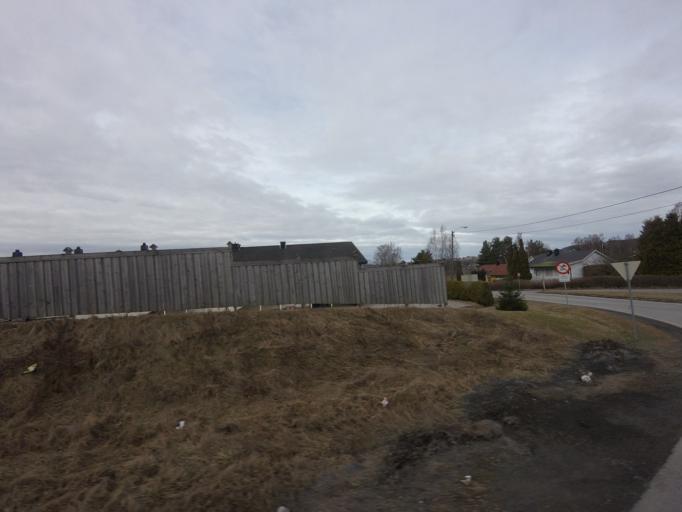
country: NO
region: Akershus
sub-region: Fet
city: Fetsund
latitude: 59.9203
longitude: 11.1832
